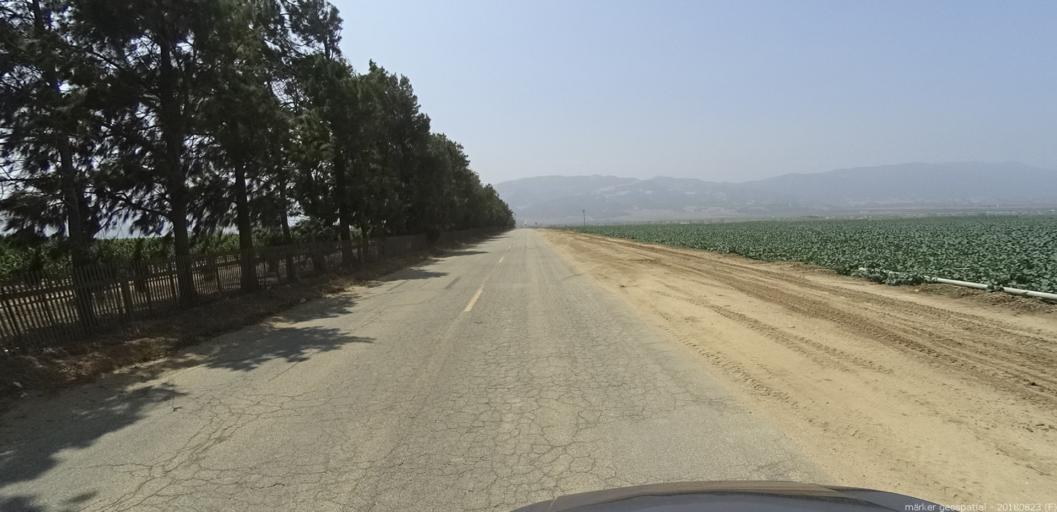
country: US
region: California
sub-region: Monterey County
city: Greenfield
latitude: 36.3304
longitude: -121.2757
